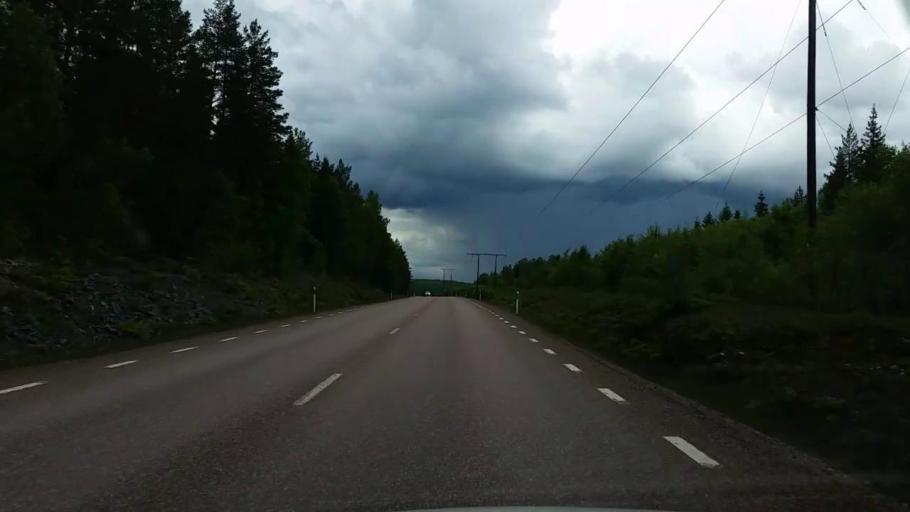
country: SE
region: Gaevleborg
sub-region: Hofors Kommun
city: Hofors
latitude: 60.5296
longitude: 16.4555
